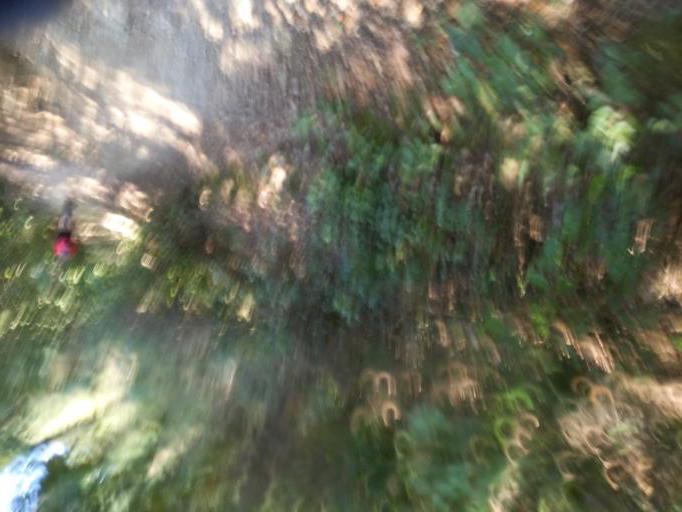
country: ES
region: Catalonia
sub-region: Provincia de Barcelona
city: Cerdanyola del Valles
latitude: 41.4711
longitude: 2.1289
